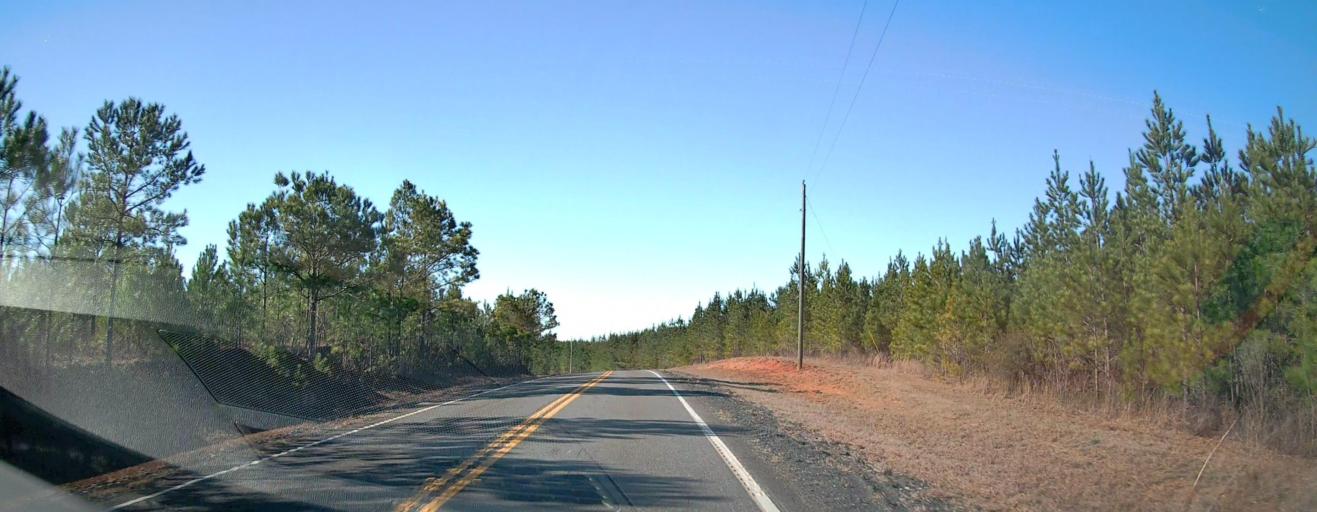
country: US
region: Georgia
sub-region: Talbot County
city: Talbotton
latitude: 32.6488
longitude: -84.3890
